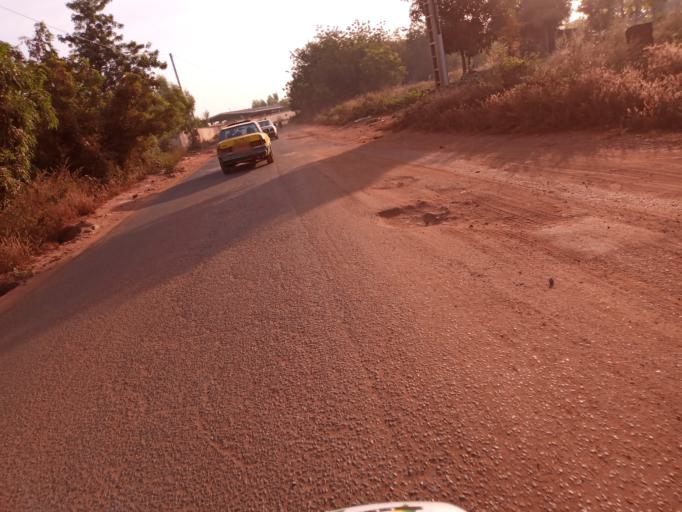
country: ML
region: Bamako
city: Bamako
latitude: 12.6361
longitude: -7.9270
